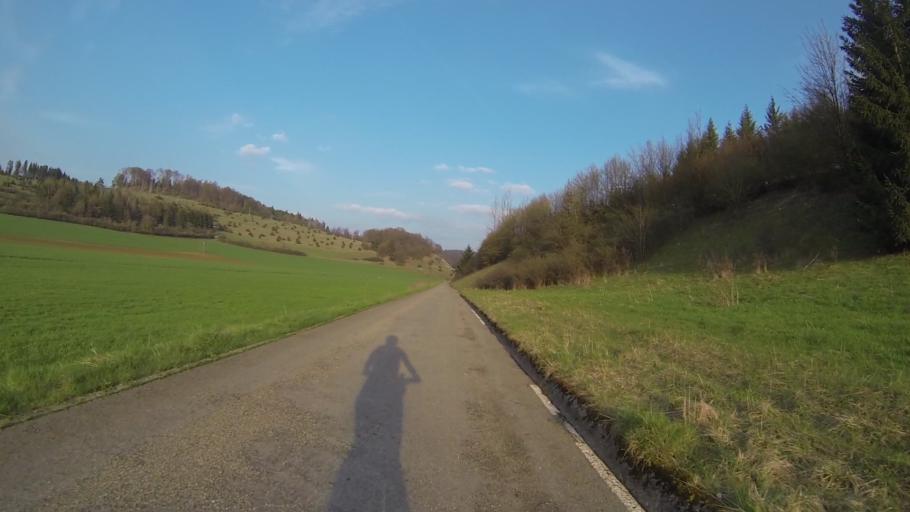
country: DE
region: Baden-Wuerttemberg
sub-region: Regierungsbezirk Stuttgart
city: Heidenheim an der Brenz
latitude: 48.6961
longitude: 10.1891
